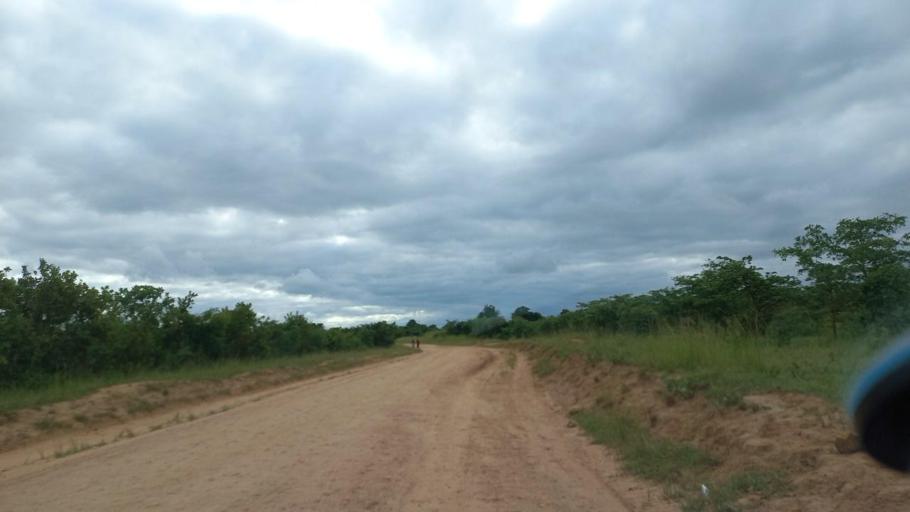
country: ZM
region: Lusaka
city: Chongwe
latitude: -15.4493
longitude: 28.8412
